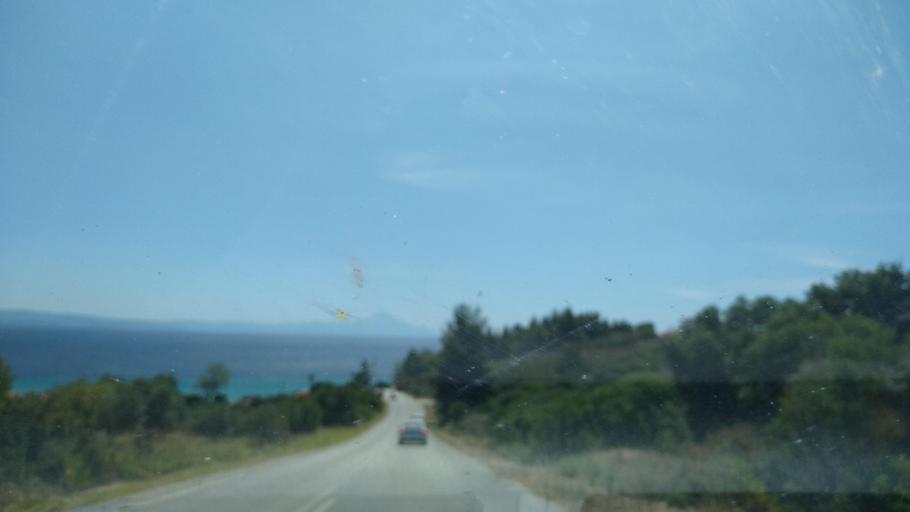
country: GR
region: Central Macedonia
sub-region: Nomos Chalkidikis
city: Agios Nikolaos
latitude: 40.3035
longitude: 23.6903
